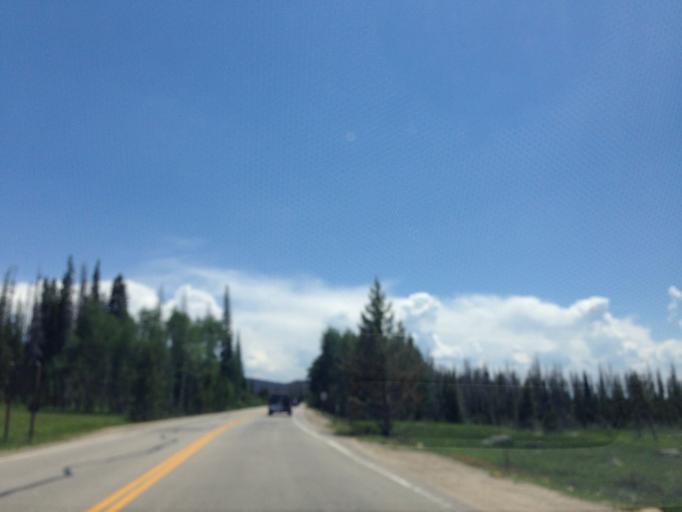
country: US
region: Colorado
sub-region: Grand County
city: Granby
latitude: 40.2711
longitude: -105.8347
